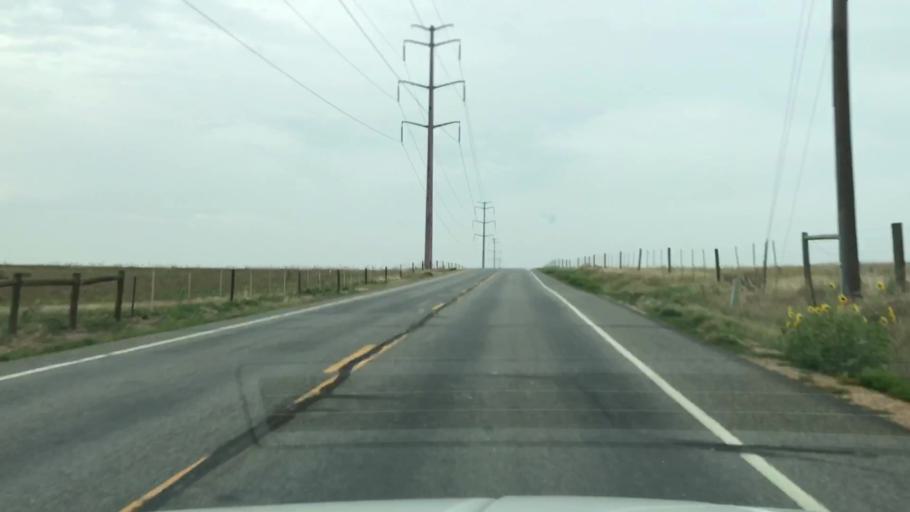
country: US
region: Colorado
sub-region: Boulder County
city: Gunbarrel
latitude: 40.0727
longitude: -105.1598
